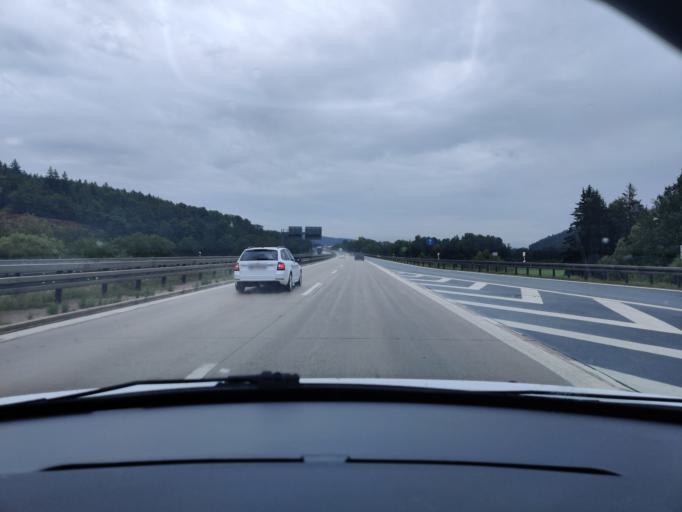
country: DE
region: Bavaria
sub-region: Upper Palatinate
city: Wernberg-Koblitz
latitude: 49.5152
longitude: 12.1672
